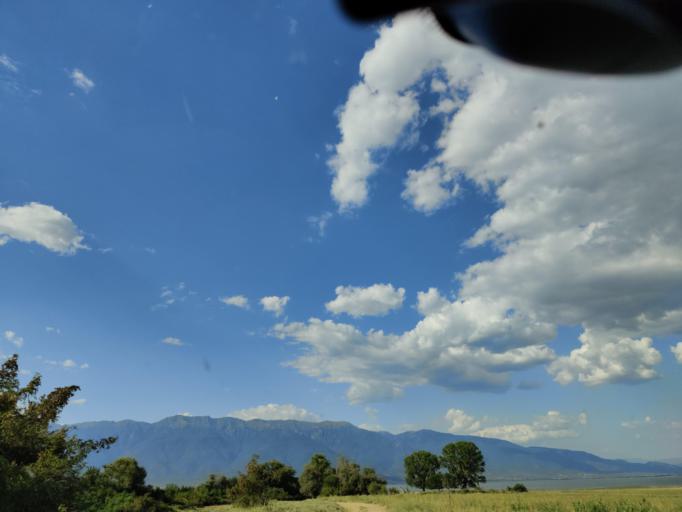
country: GR
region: Central Macedonia
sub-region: Nomos Serron
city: Chrysochorafa
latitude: 41.1850
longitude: 23.1078
